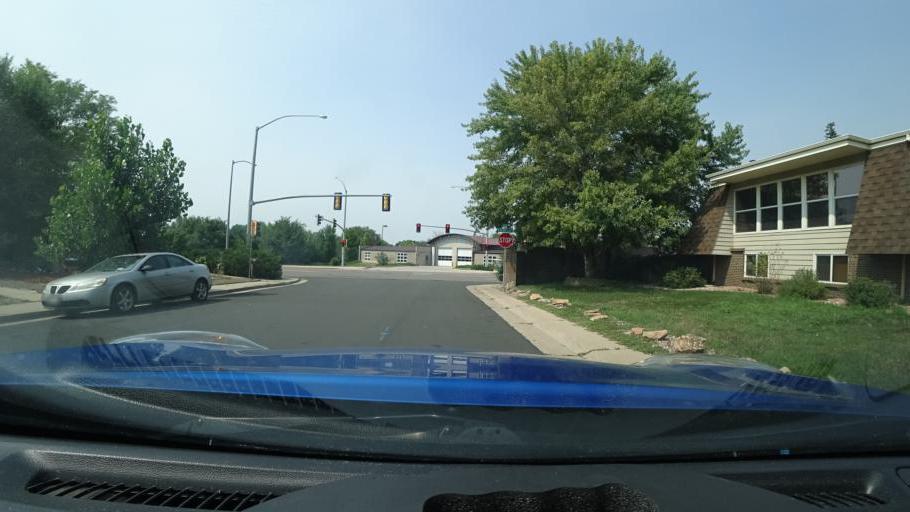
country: US
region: Colorado
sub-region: Adams County
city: Aurora
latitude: 39.6744
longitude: -104.8620
